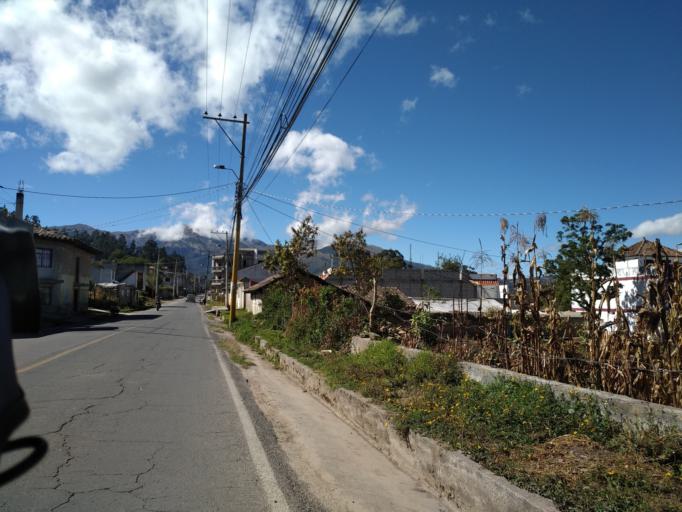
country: EC
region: Imbabura
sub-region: Canton Otavalo
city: Otavalo
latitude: 0.2157
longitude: -78.2147
